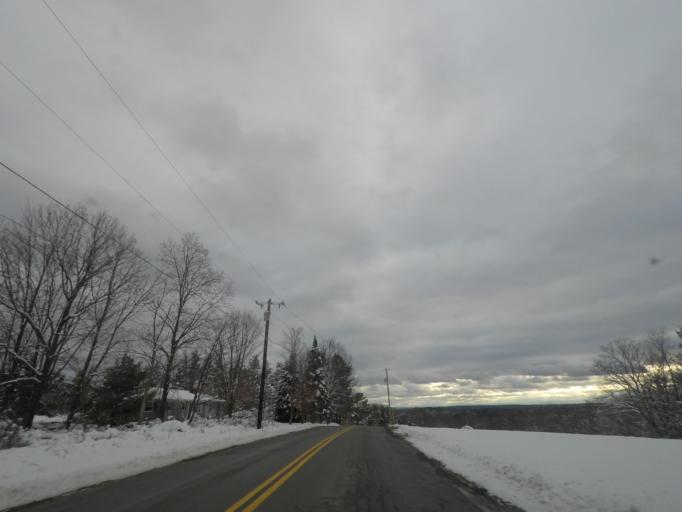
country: US
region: New York
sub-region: Rensselaer County
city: Averill Park
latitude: 42.6611
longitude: -73.5209
